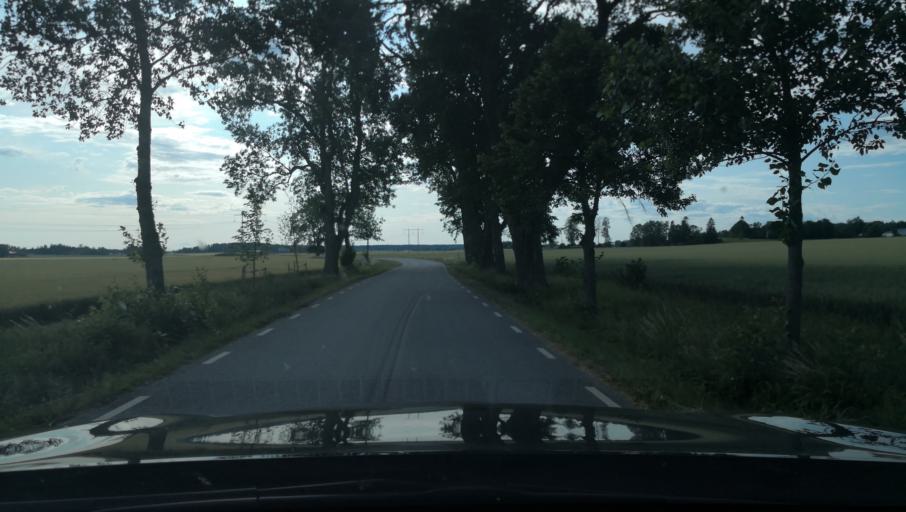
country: SE
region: Uppsala
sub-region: Enkopings Kommun
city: Orsundsbro
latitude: 59.6978
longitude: 17.3181
